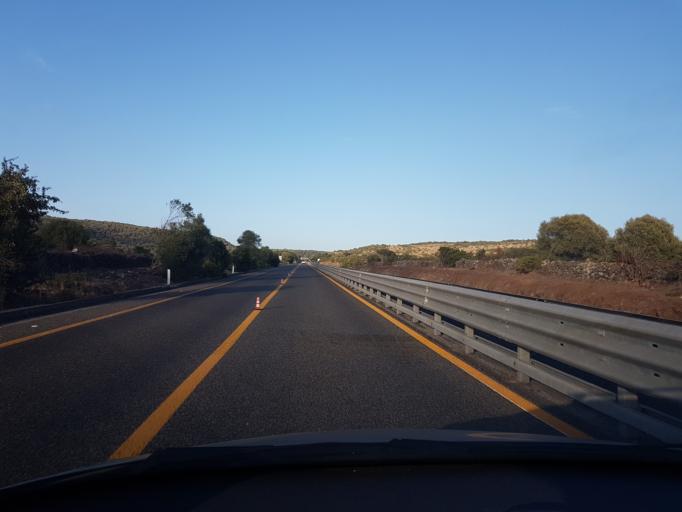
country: IT
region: Sardinia
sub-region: Provincia di Oristano
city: Bauladu
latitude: 40.0366
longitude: 8.6824
